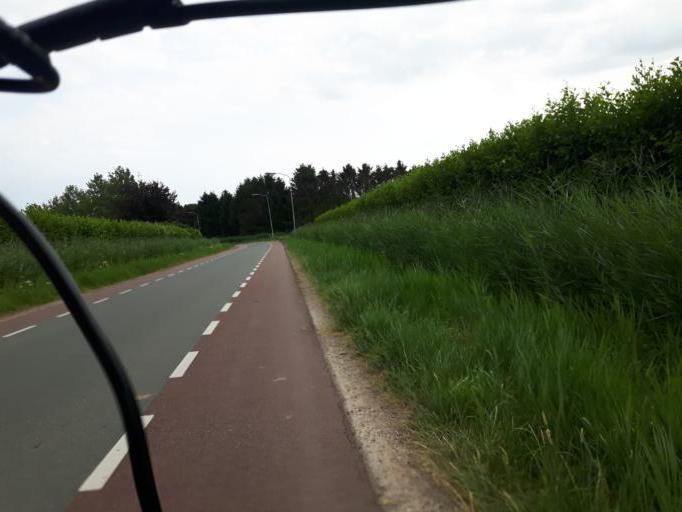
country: NL
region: Gelderland
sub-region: Gemeente Maasdriel
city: Heerewaarden
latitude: 51.8711
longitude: 5.3729
